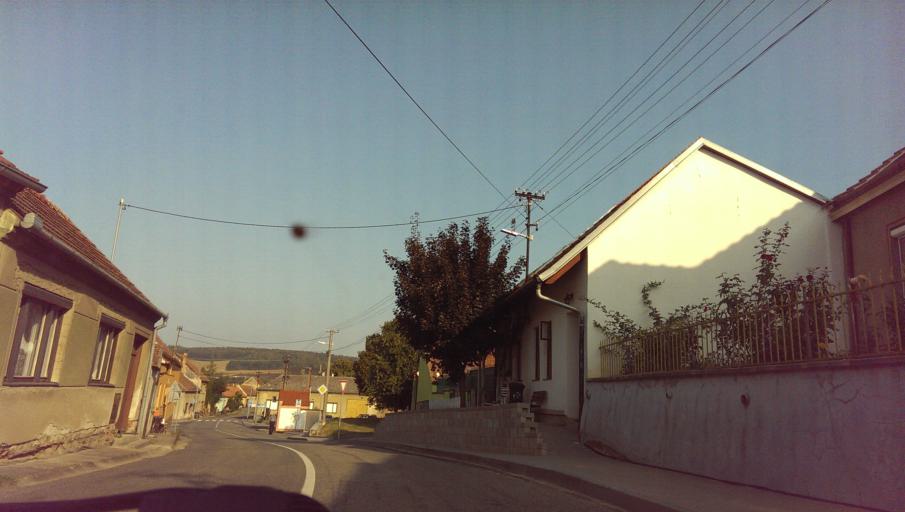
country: CZ
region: Zlin
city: Korycany
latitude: 49.1294
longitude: 17.1258
